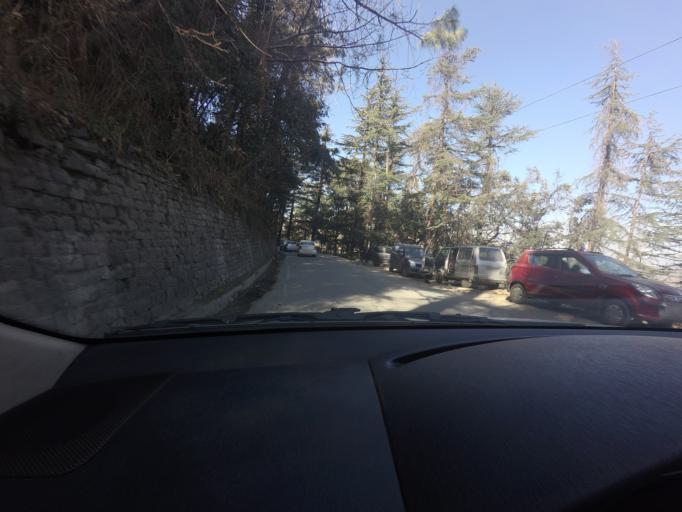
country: IN
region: Himachal Pradesh
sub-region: Shimla
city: Shimla
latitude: 31.1080
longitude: 77.1830
